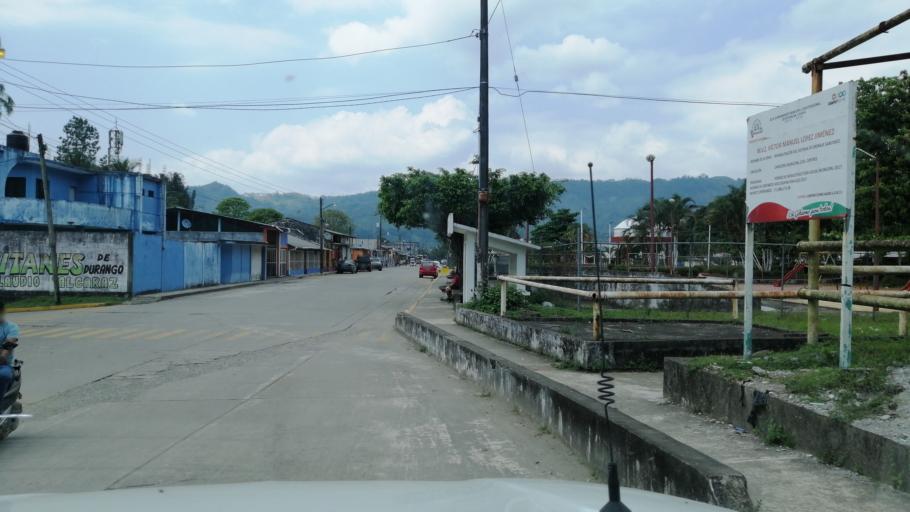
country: MX
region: Chiapas
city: Ostuacan
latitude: 17.4061
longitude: -93.3347
